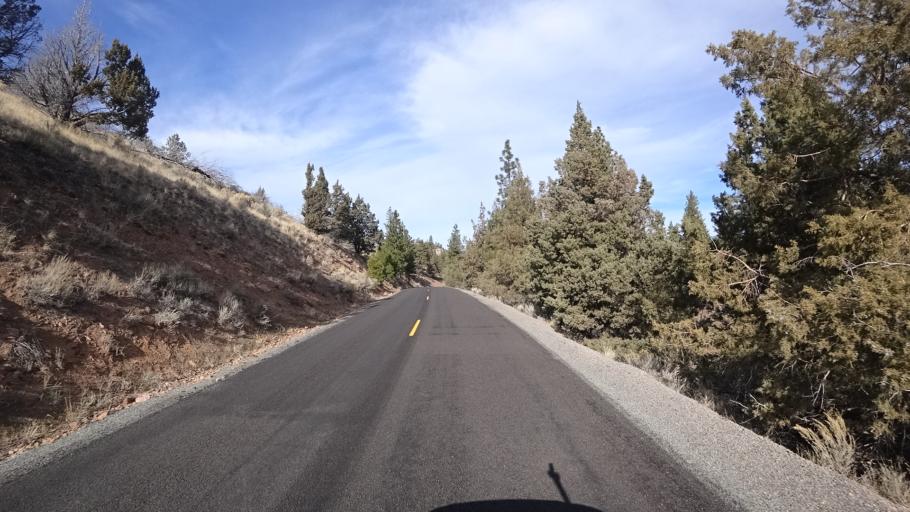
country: US
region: California
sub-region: Siskiyou County
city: Weed
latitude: 41.5018
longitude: -122.3901
